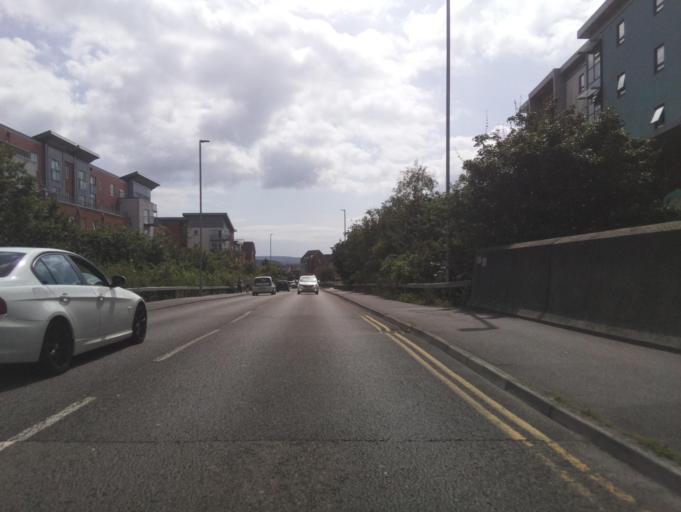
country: GB
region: England
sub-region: Poole
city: Poole
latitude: 50.7158
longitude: -1.9769
